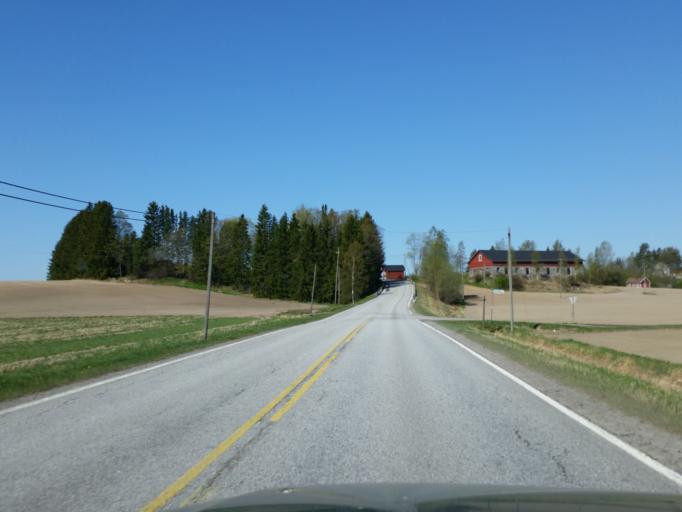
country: FI
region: Uusimaa
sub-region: Helsinki
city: Siuntio
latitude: 60.1755
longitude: 24.1472
